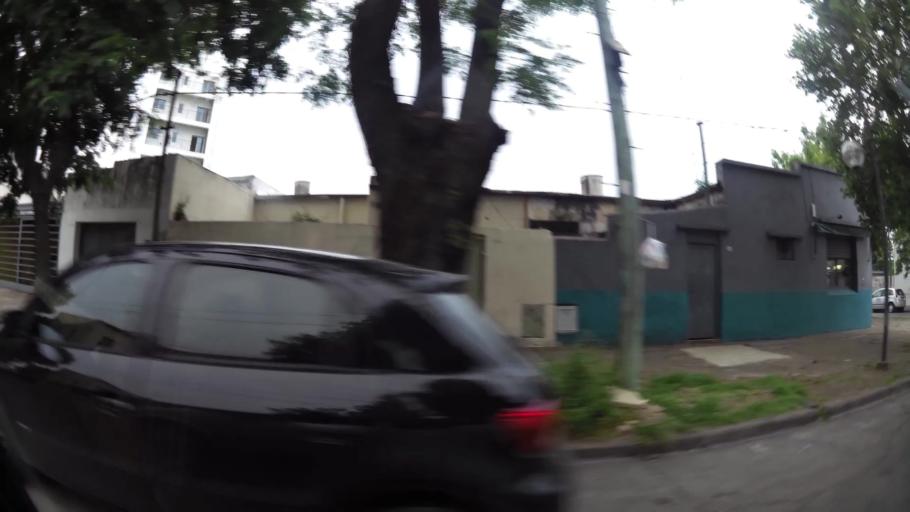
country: AR
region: Buenos Aires
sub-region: Partido de La Plata
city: La Plata
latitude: -34.9216
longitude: -57.9751
